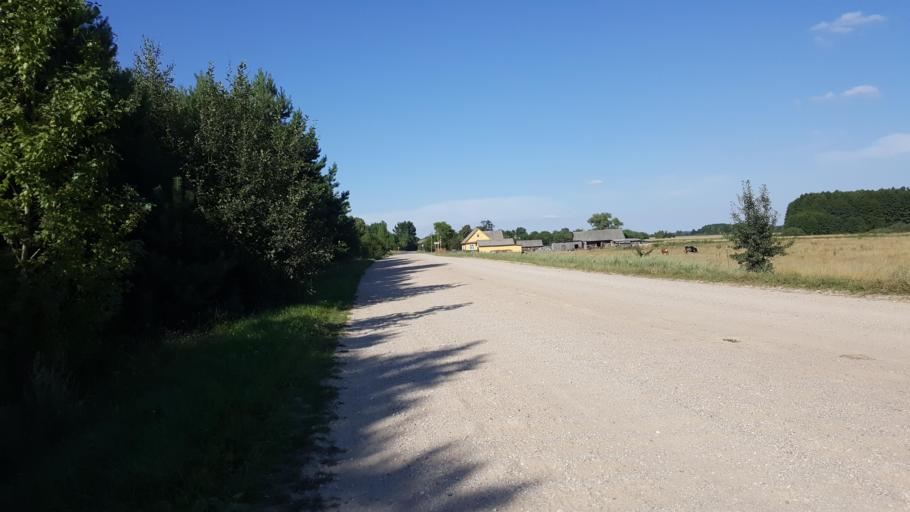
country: BY
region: Brest
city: Kamyanyets
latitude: 52.3743
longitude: 23.7323
